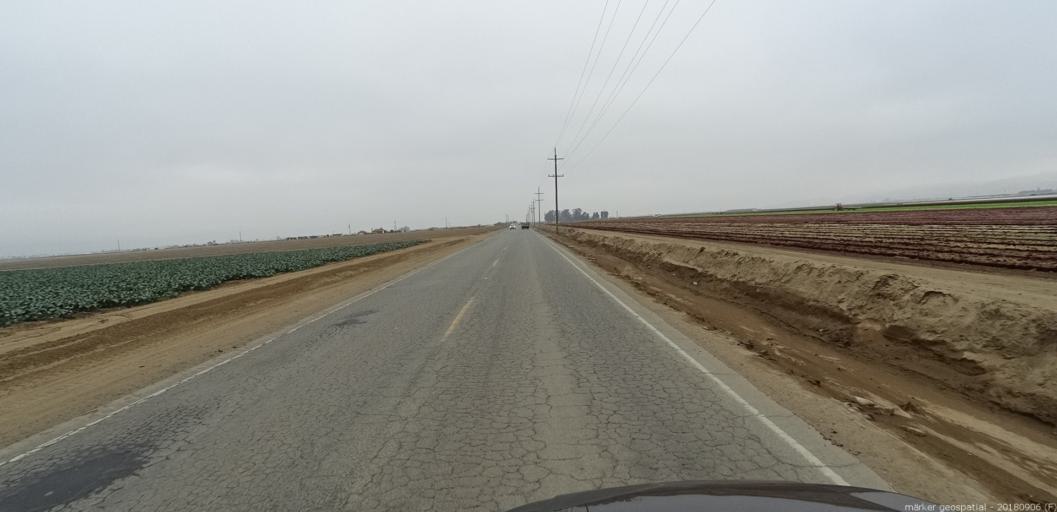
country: US
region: California
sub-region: Monterey County
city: Salinas
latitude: 36.6523
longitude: -121.5829
